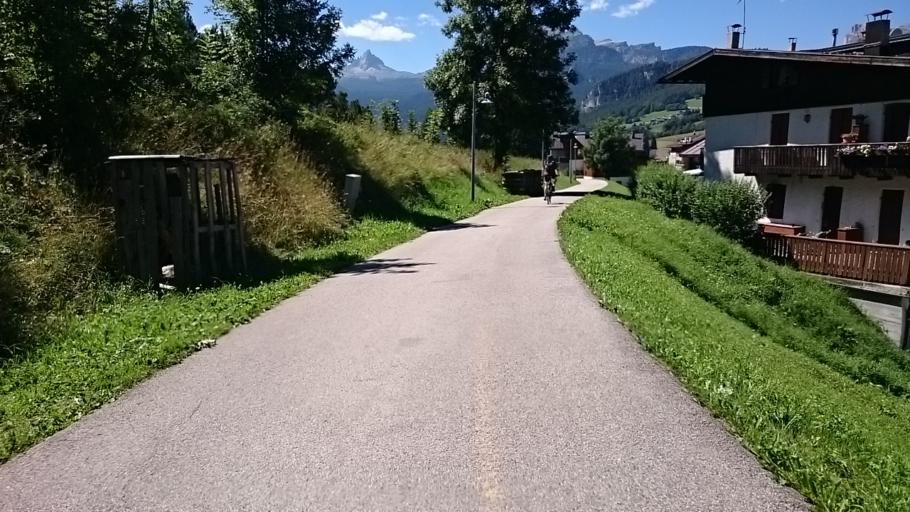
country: IT
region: Veneto
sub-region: Provincia di Belluno
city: Cortina d'Ampezzo
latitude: 46.5439
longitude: 12.1373
